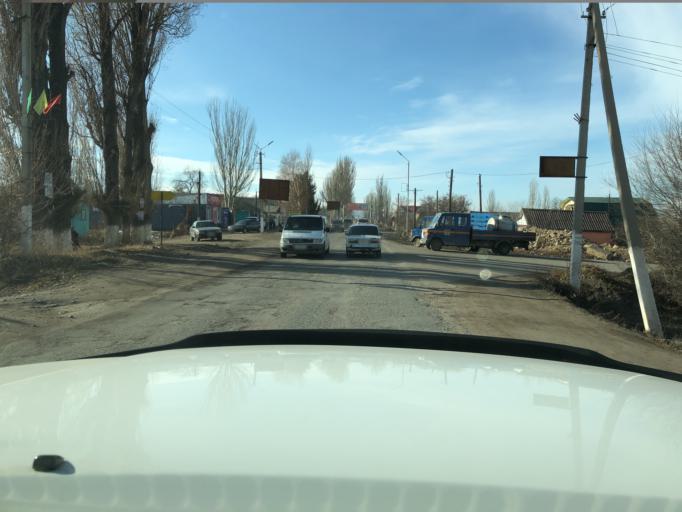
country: KG
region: Ysyk-Koel
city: Pokrovka
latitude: 42.3372
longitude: 77.9941
